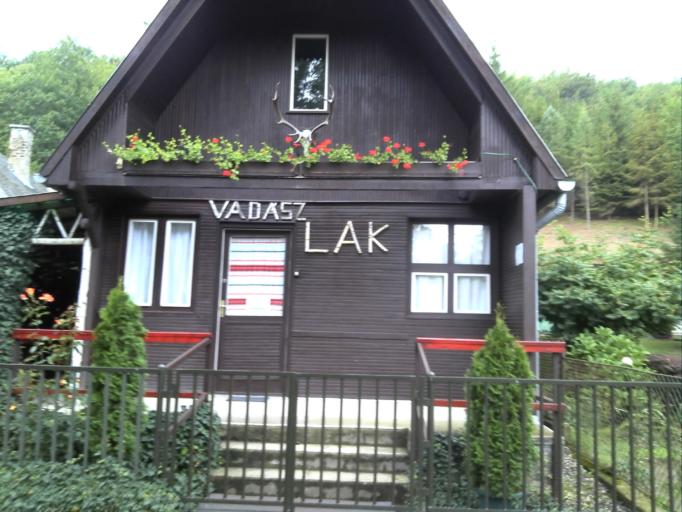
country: HU
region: Borsod-Abauj-Zemplen
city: Satoraljaujhely
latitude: 48.4092
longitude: 21.6066
